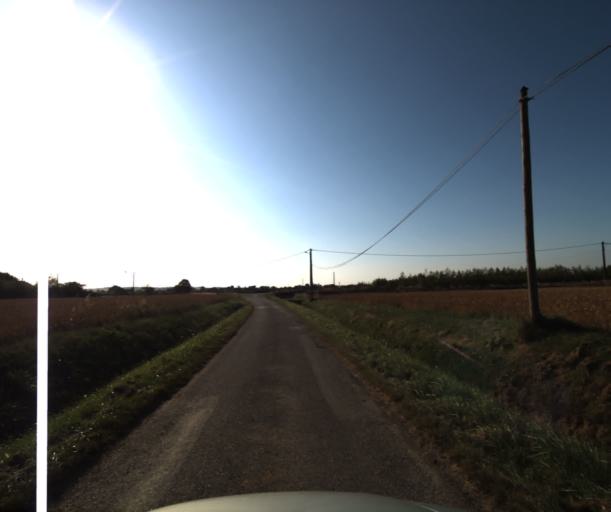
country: FR
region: Midi-Pyrenees
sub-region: Departement de la Haute-Garonne
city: Labarthe-sur-Leze
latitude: 43.4493
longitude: 1.3867
